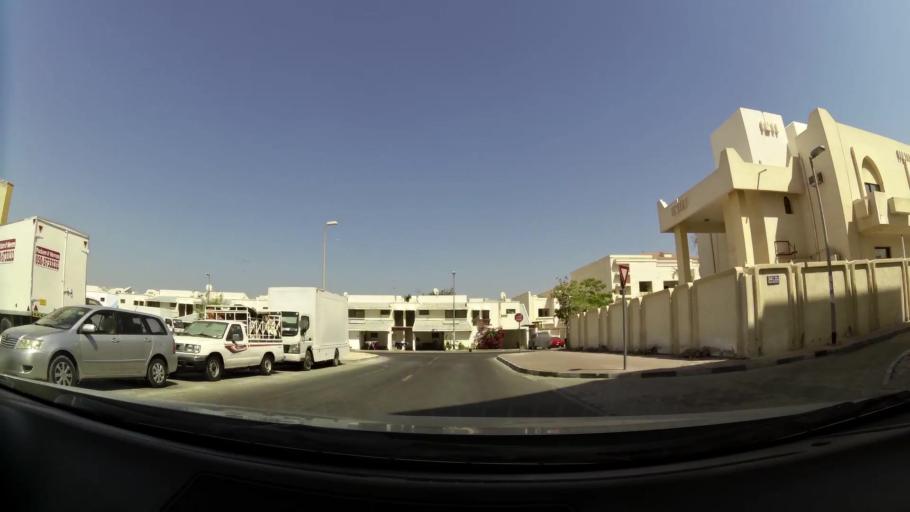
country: AE
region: Ash Shariqah
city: Sharjah
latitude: 25.2322
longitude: 55.2741
